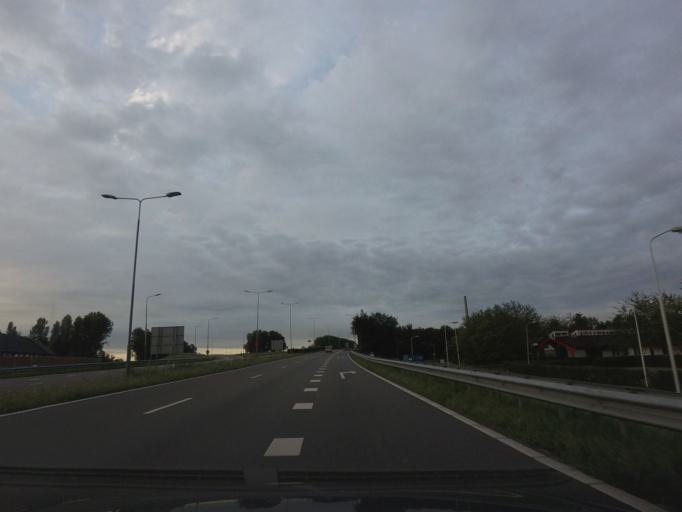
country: NL
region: North Holland
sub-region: Gemeente Zaanstad
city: Zaanstad
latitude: 52.4965
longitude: 4.7766
